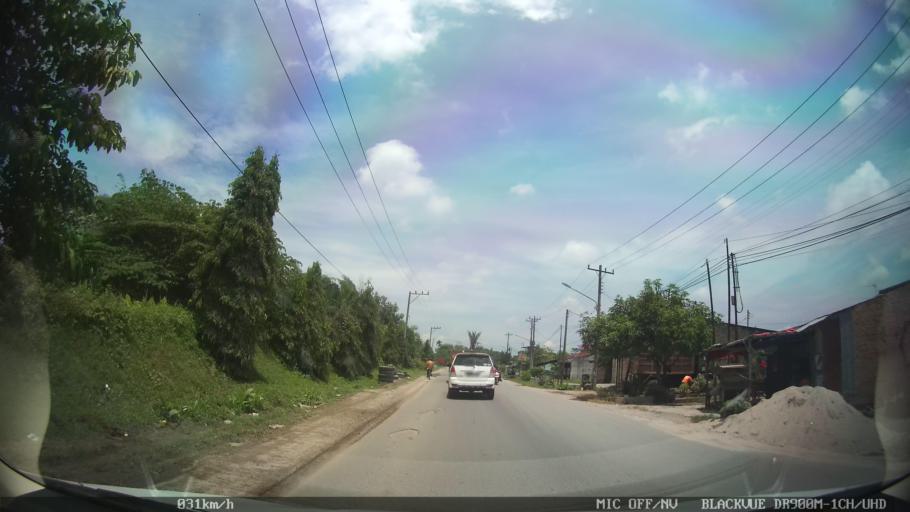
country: ID
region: North Sumatra
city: Perbaungan
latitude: 3.5364
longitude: 98.8841
